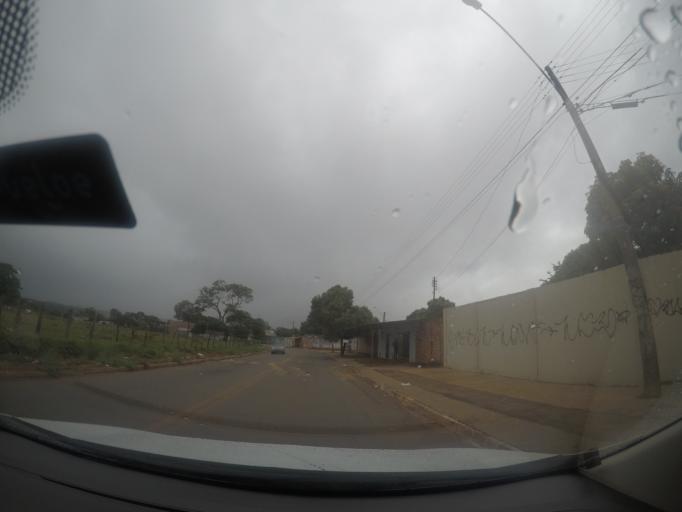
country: BR
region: Goias
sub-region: Goiania
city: Goiania
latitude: -16.6149
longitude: -49.3524
